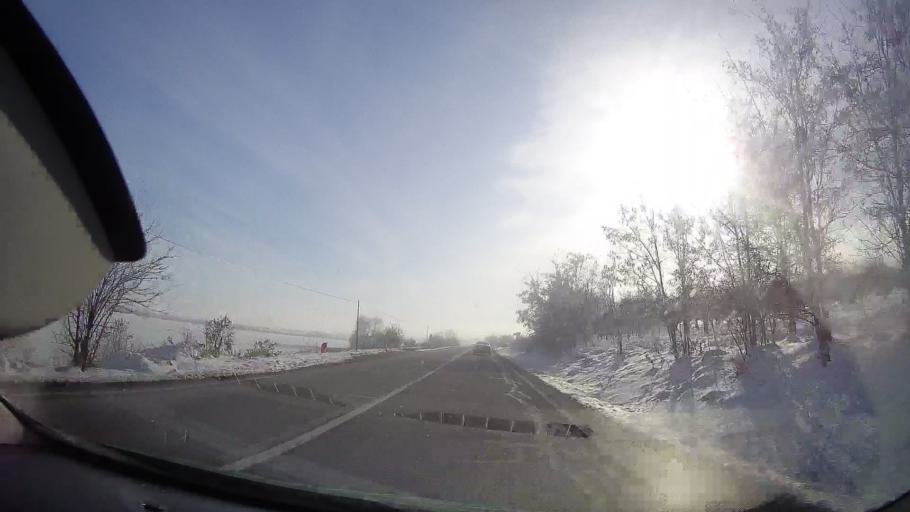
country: RO
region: Neamt
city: Bodesti
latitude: 47.0097
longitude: 26.4244
